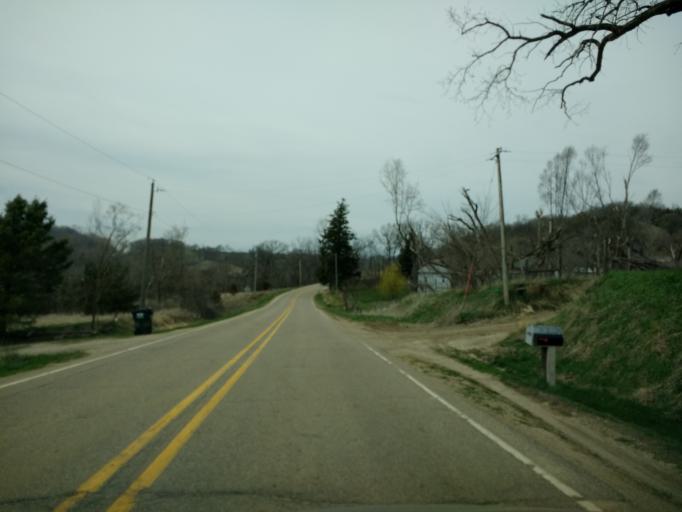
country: US
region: Iowa
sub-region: Monona County
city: Mapleton
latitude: 42.2339
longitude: -95.9428
